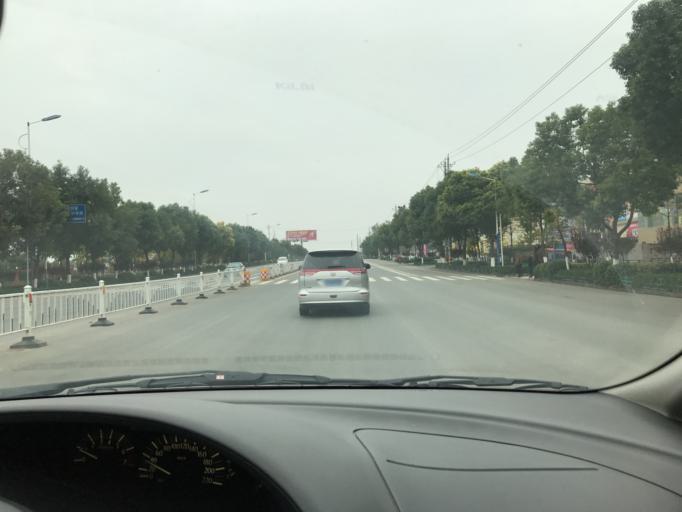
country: CN
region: Hubei
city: Anlu
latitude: 31.2499
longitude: 113.6958
